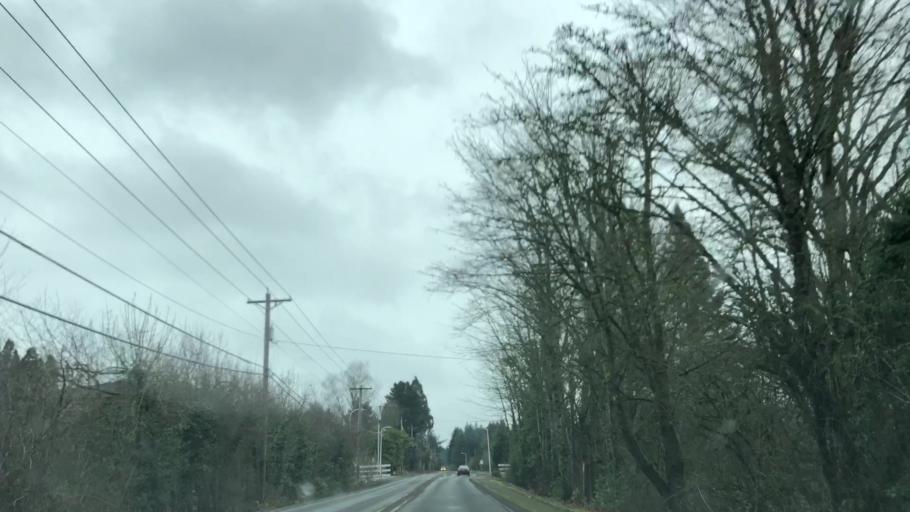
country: US
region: Oregon
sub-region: Washington County
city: West Haven
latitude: 45.5275
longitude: -122.7771
